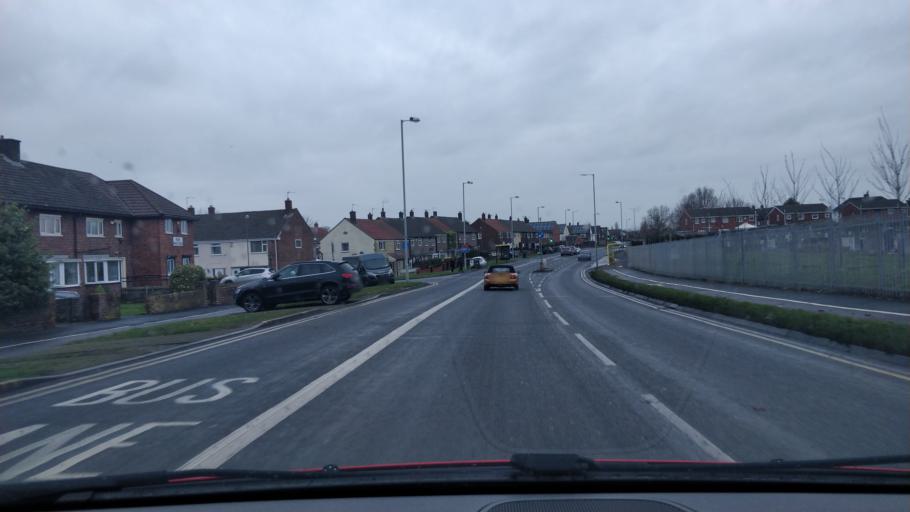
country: GB
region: England
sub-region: Sefton
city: Litherland
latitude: 53.4812
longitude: -2.9965
